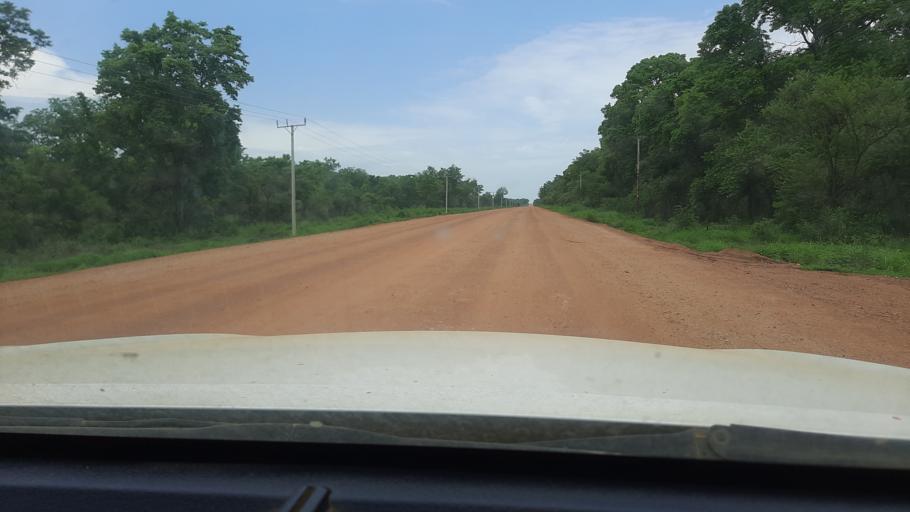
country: ET
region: Gambela
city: Gambela
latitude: 8.1338
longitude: 34.5789
